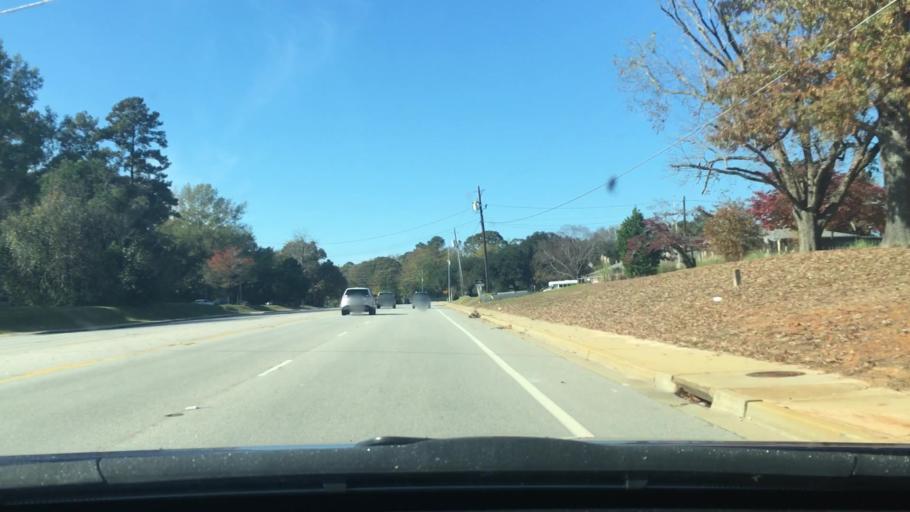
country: US
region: South Carolina
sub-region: Sumter County
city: South Sumter
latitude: 33.9037
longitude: -80.3844
